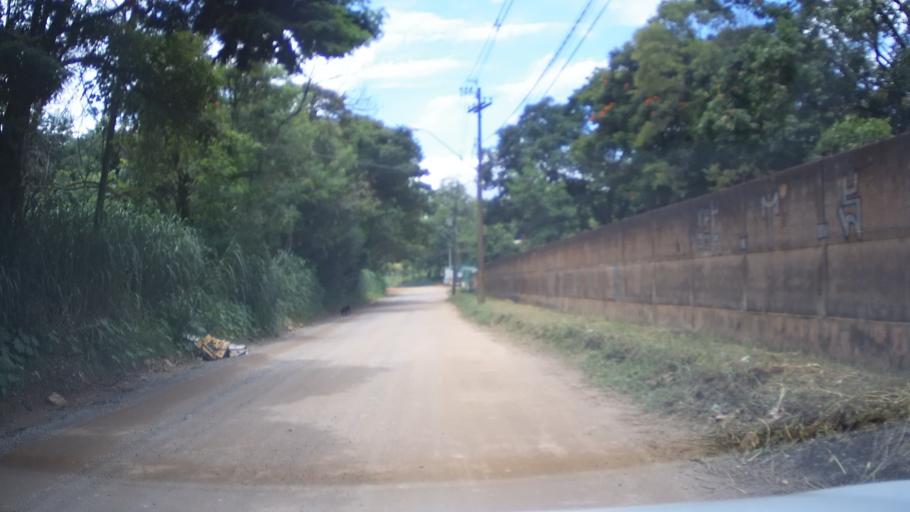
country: BR
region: Sao Paulo
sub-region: Valinhos
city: Valinhos
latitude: -22.9917
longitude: -46.9884
